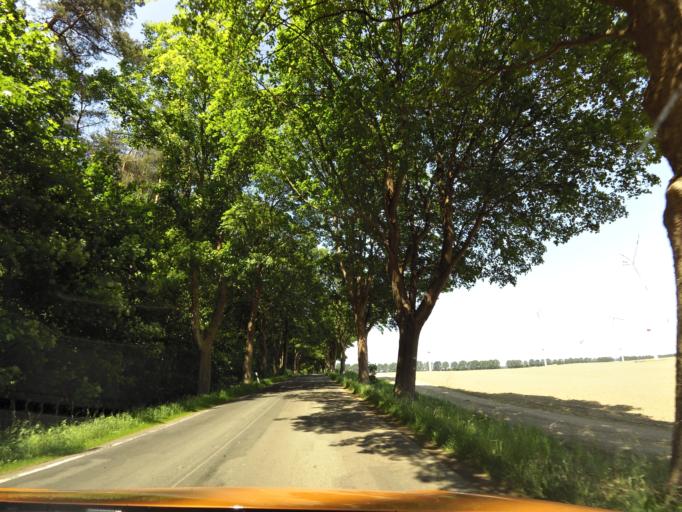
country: DE
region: Mecklenburg-Vorpommern
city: Neuburg
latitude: 53.4105
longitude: 11.8959
